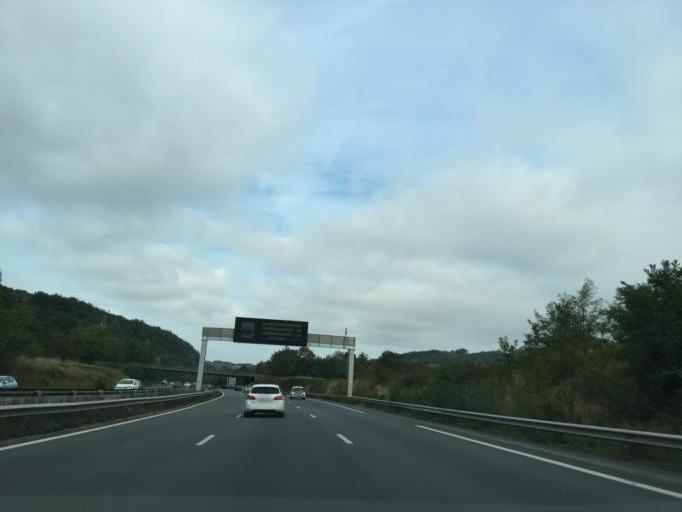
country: FR
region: Rhone-Alpes
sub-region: Departement de la Loire
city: La Fouillouse
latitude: 45.4936
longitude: 4.3182
